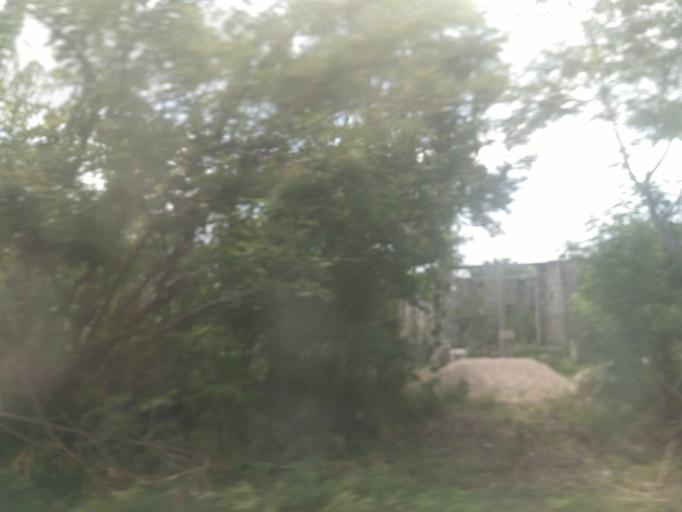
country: TZ
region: Zanzibar Urban/West
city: Zanzibar
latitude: -6.2874
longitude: 39.2850
